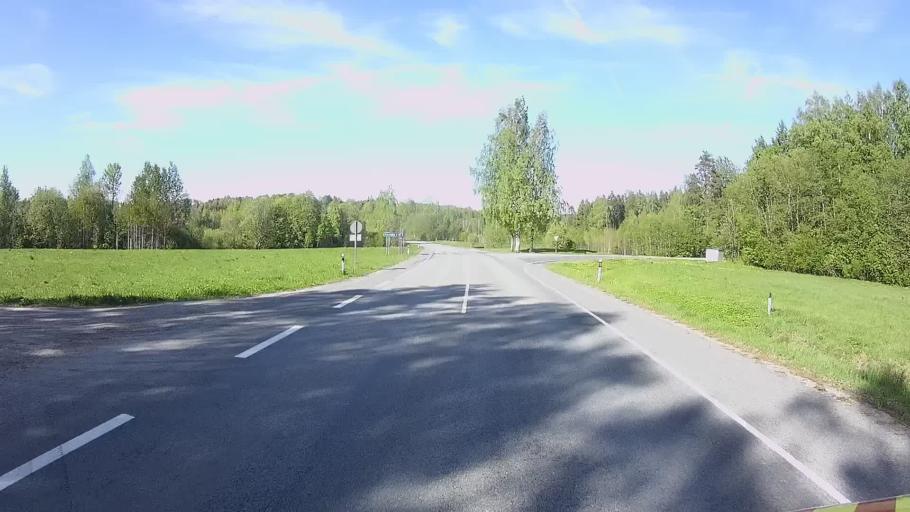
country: EE
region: Vorumaa
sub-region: Antsla vald
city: Vana-Antsla
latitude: 57.9581
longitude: 26.4512
